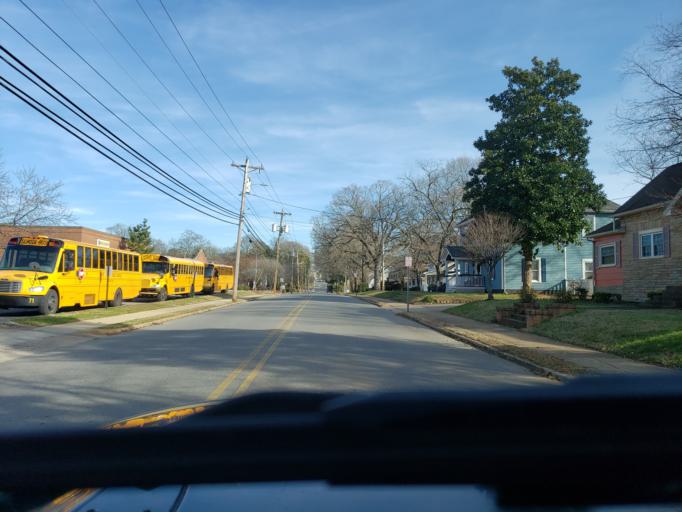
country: US
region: North Carolina
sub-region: Cleveland County
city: Kings Mountain
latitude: 35.2394
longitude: -81.3527
